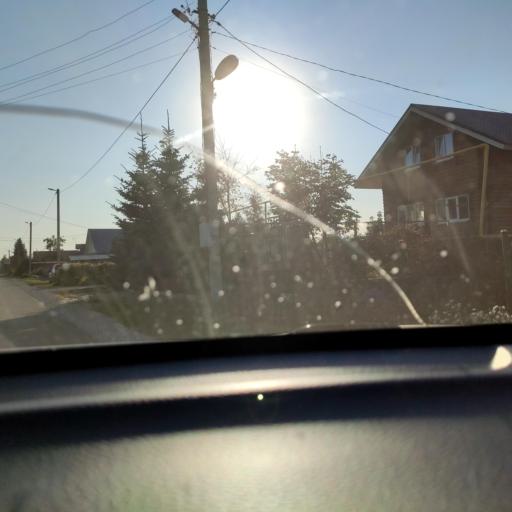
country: RU
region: Tatarstan
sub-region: Gorod Kazan'
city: Kazan
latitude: 55.7287
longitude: 49.1497
